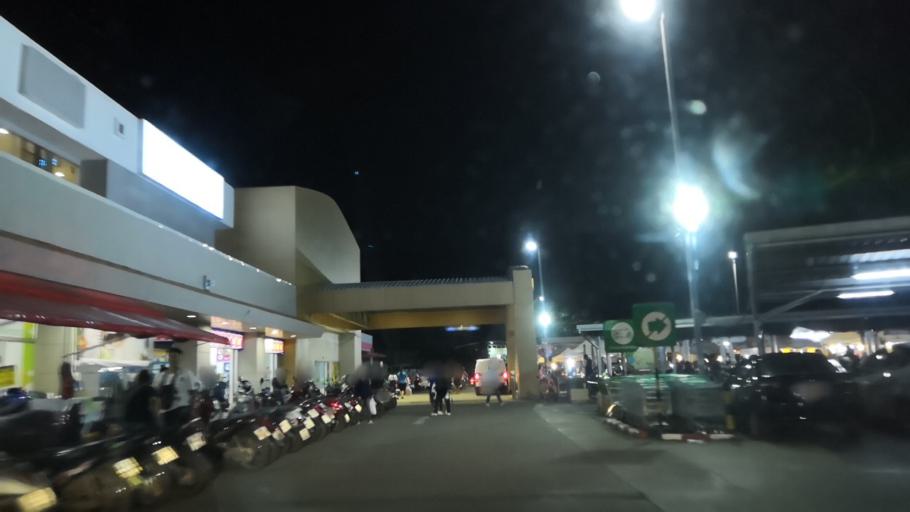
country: TH
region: Chiang Mai
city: Chiang Mai
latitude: 18.7591
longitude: 98.9722
